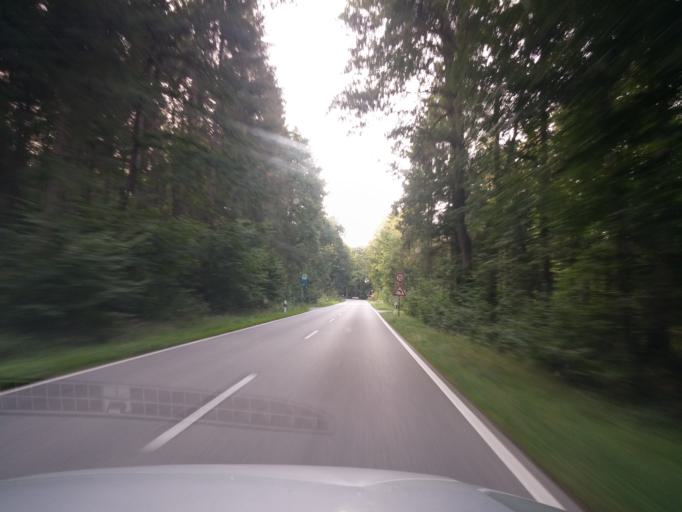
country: DE
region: Bavaria
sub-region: Upper Bavaria
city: Grasbrunn
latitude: 48.0701
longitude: 11.7735
